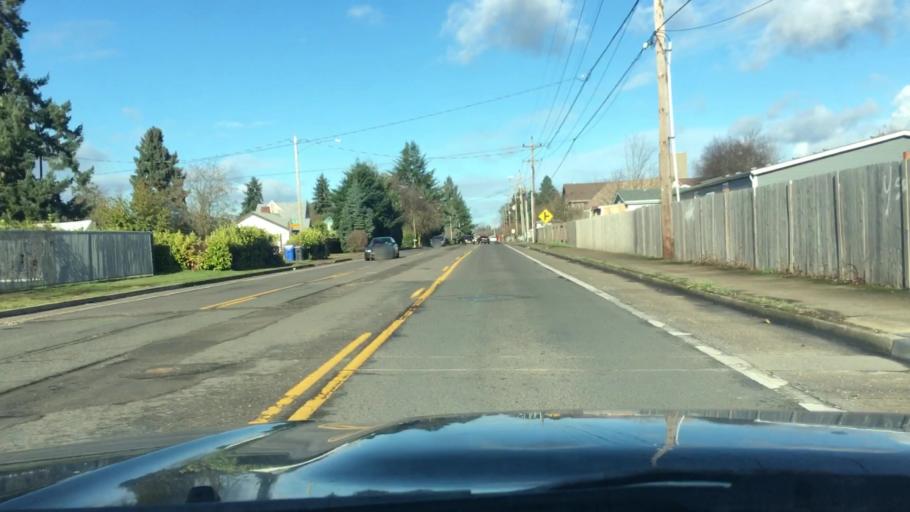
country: US
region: Oregon
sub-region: Lane County
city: Eugene
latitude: 44.0651
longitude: -123.1631
